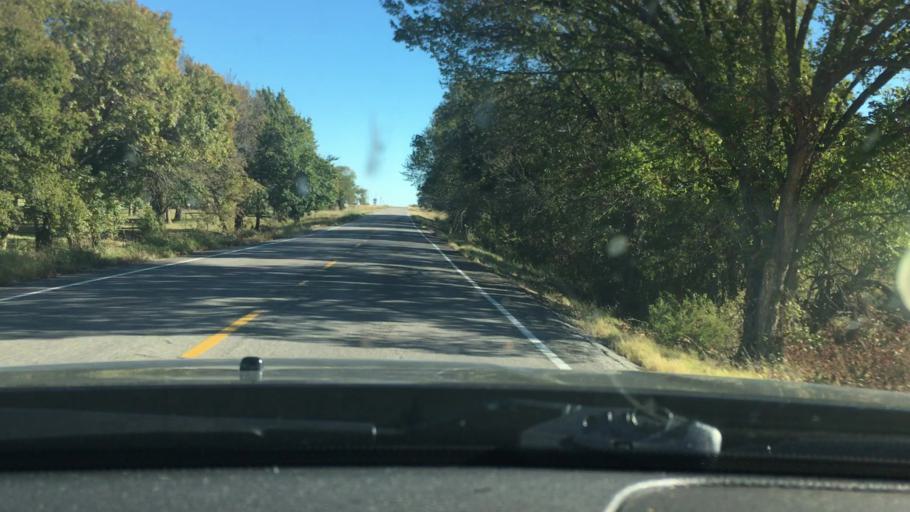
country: US
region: Oklahoma
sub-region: Marshall County
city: Madill
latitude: 34.1273
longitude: -96.7248
